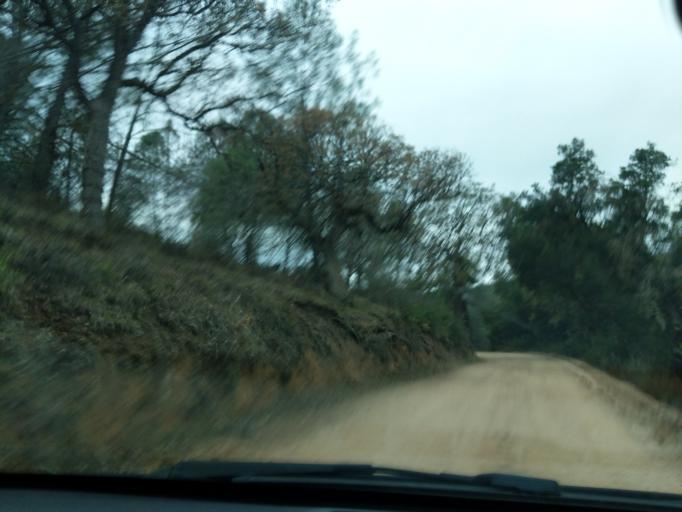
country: US
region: California
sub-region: Monterey County
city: Soledad
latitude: 36.5634
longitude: -121.2276
